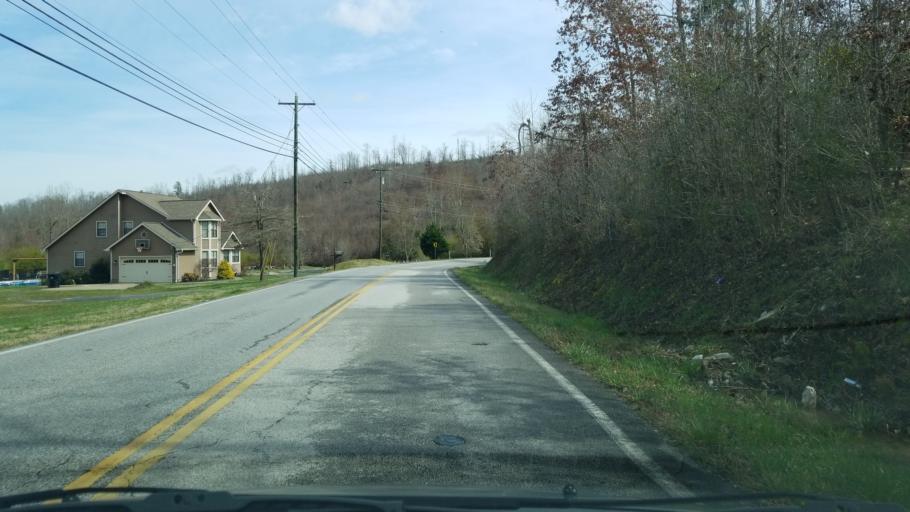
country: US
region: Tennessee
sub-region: Hamilton County
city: Harrison
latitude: 35.1424
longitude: -85.0984
